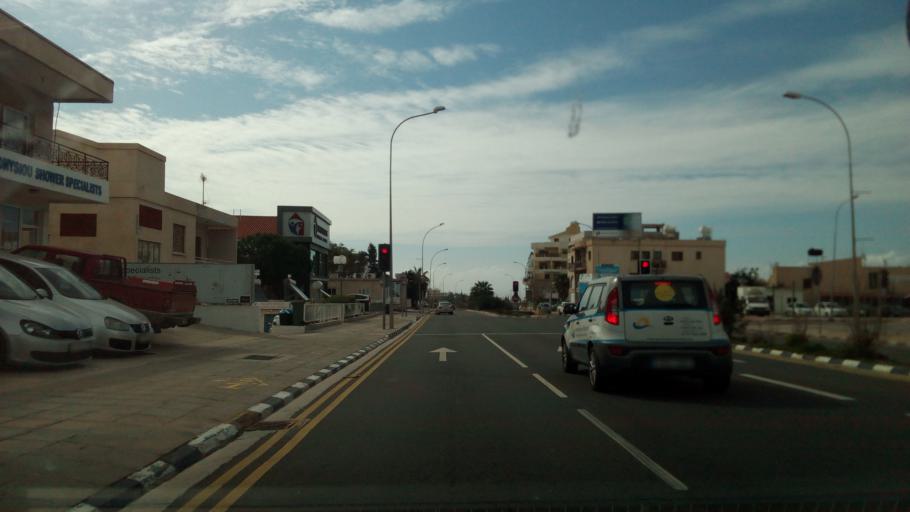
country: CY
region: Pafos
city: Paphos
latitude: 34.7742
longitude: 32.4427
